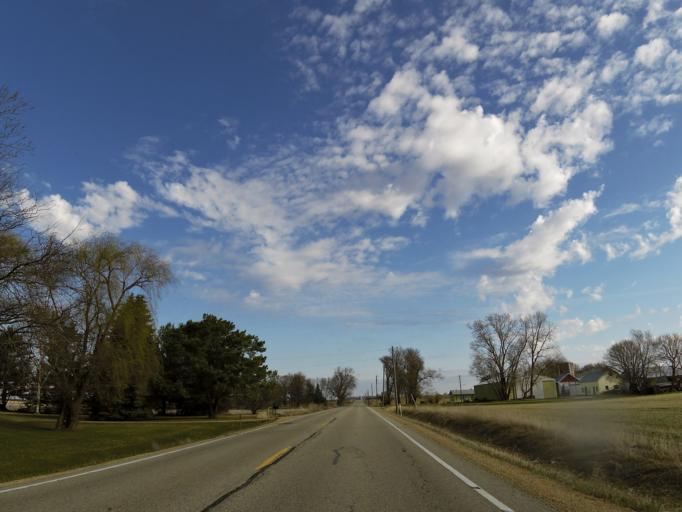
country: US
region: Minnesota
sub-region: Washington County
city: Cottage Grove
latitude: 44.8274
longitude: -92.8627
